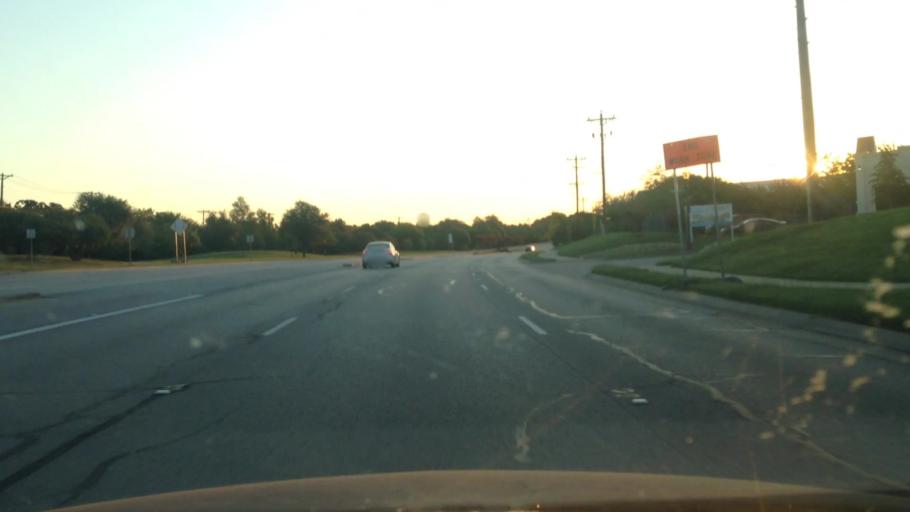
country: US
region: Texas
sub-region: Tarrant County
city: Southlake
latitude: 32.9403
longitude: -97.1817
